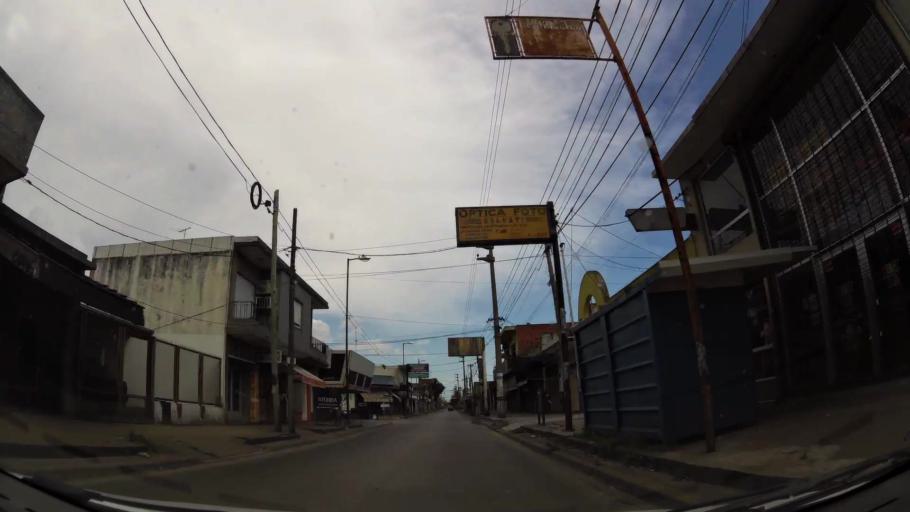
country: AR
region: Buenos Aires
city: Ituzaingo
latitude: -34.6407
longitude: -58.6883
